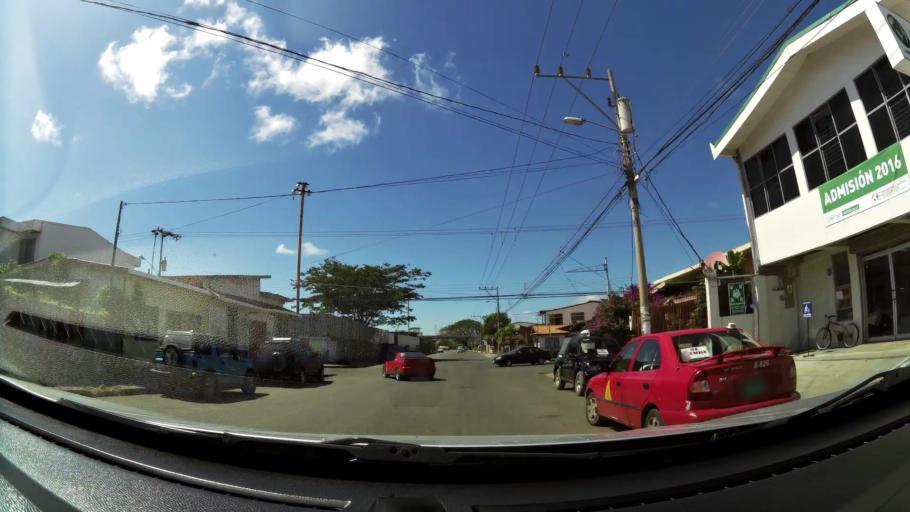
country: CR
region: Guanacaste
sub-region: Canton de Canas
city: Canas
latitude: 10.4291
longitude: -85.0929
